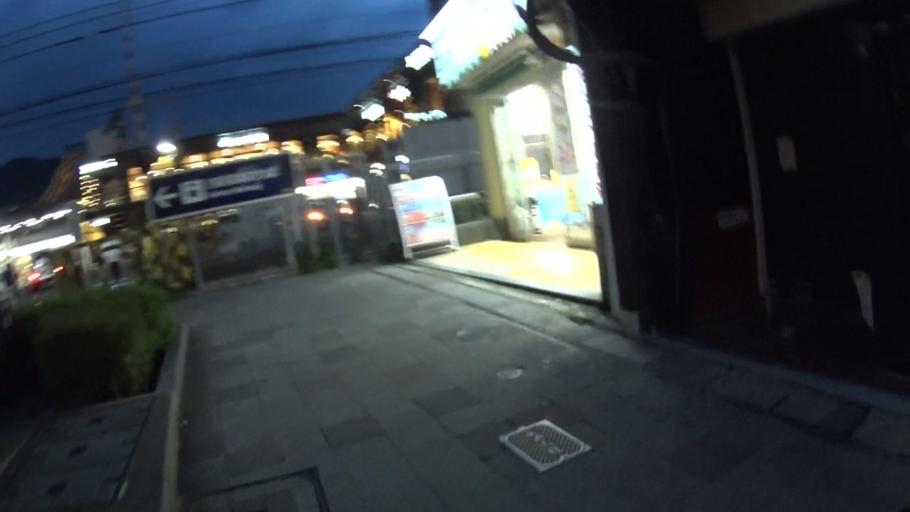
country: JP
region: Shiga Prefecture
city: Hikone
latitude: 35.2773
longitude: 136.3879
